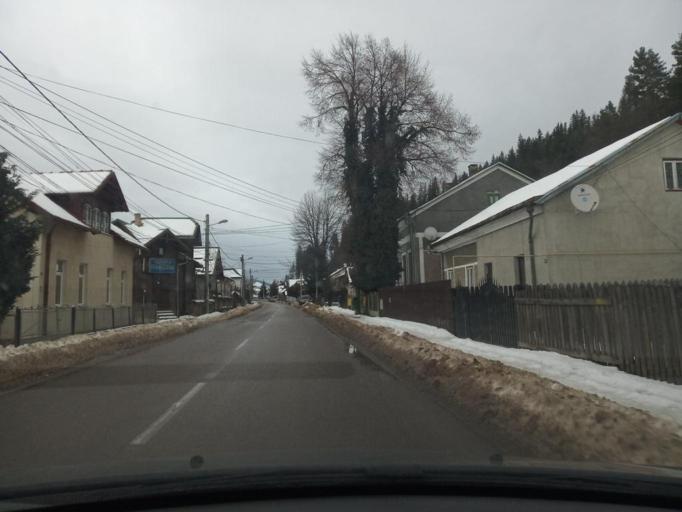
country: RO
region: Suceava
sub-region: Oras Gura Humorului
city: Gura Humorului
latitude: 47.5574
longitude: 25.8901
